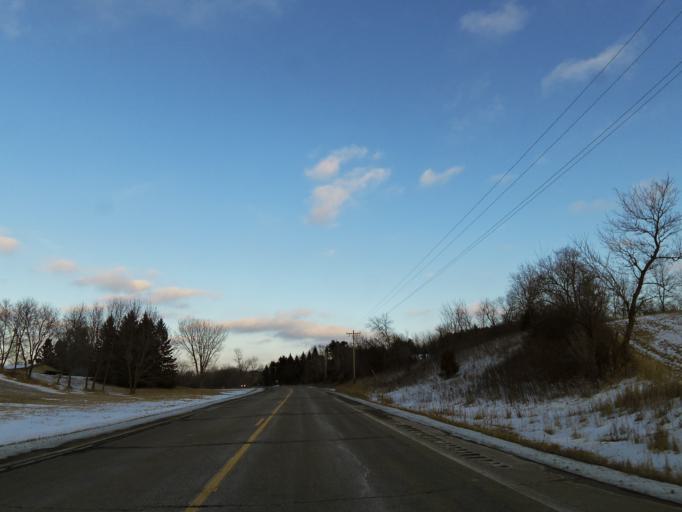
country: US
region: Minnesota
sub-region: Scott County
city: Elko New Market
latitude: 44.6373
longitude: -93.3449
